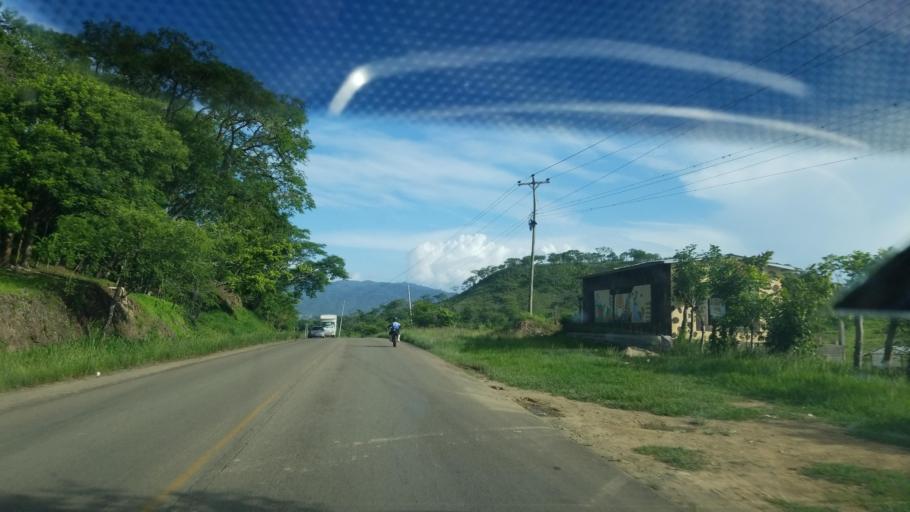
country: HN
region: El Paraiso
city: Arauli
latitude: 13.9173
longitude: -86.5575
